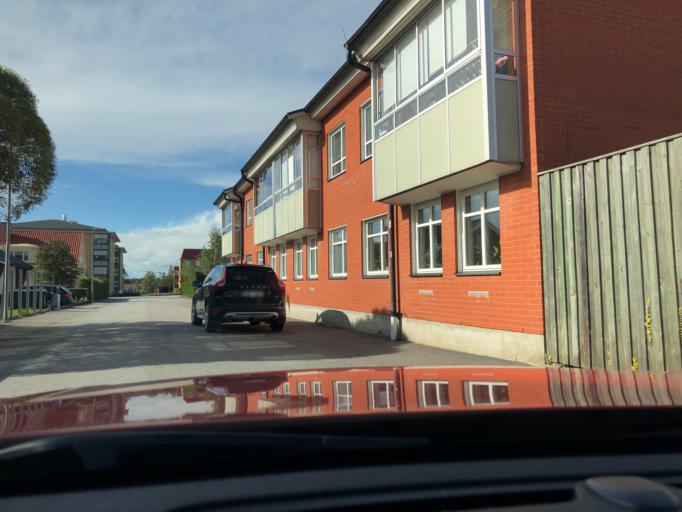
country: SE
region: Skane
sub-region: Sjobo Kommun
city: Sjoebo
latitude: 55.6345
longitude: 13.7052
